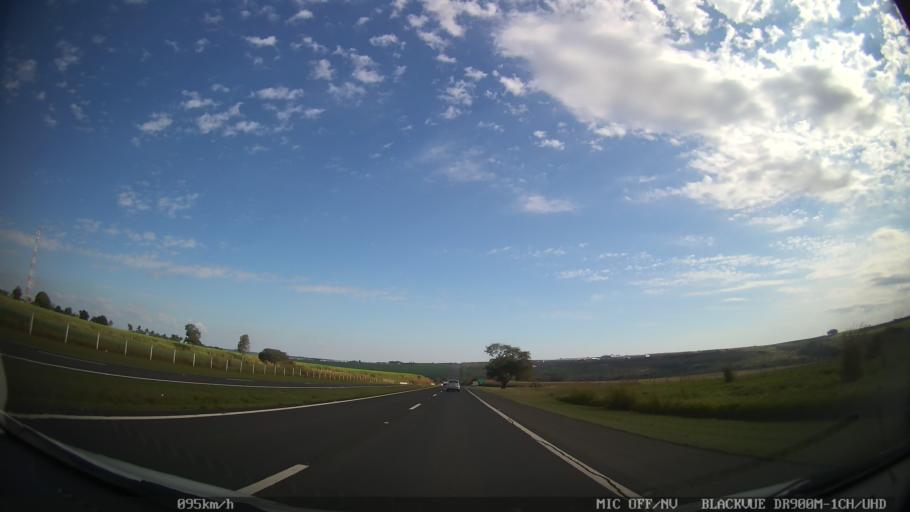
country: BR
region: Sao Paulo
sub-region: Iracemapolis
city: Iracemapolis
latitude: -22.6184
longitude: -47.4858
